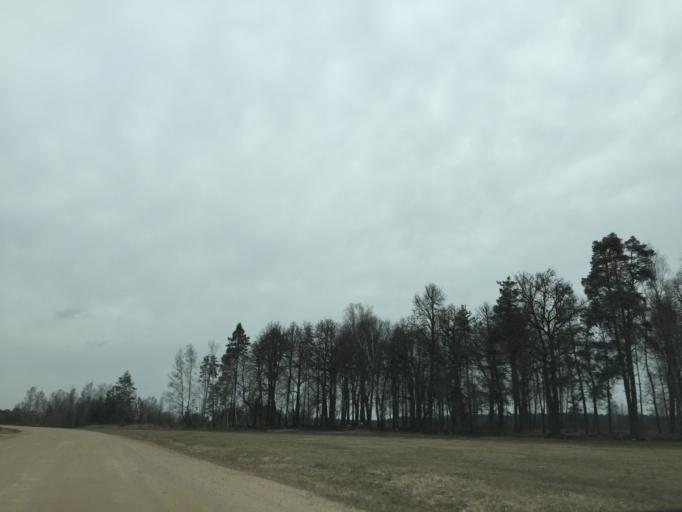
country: LV
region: Livani
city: Livani
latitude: 56.3032
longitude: 26.1706
